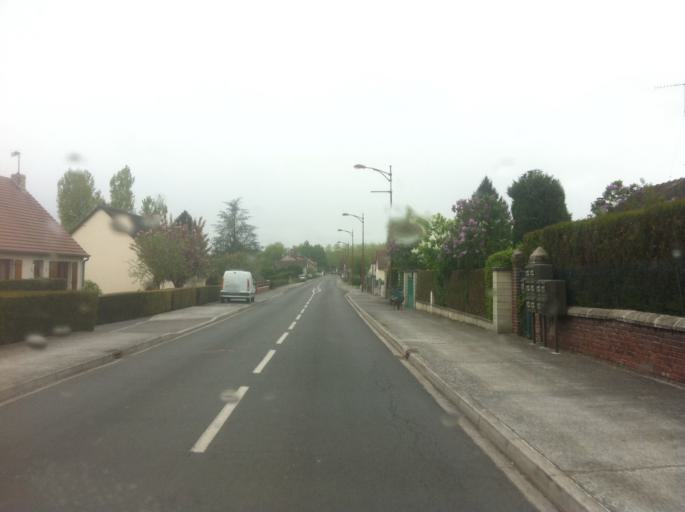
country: FR
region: Picardie
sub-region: Departement de l'Aisne
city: Coucy-le-Chateau-Auffrique
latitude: 49.5269
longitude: 3.3141
